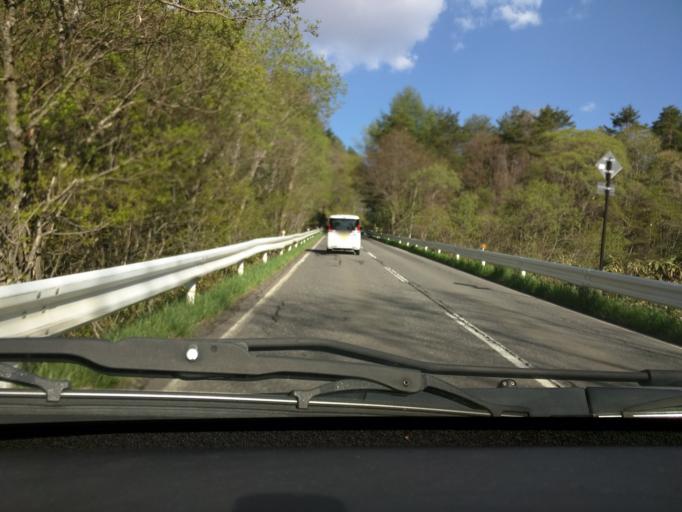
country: JP
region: Nagano
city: Nagano-shi
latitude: 36.7034
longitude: 138.1483
